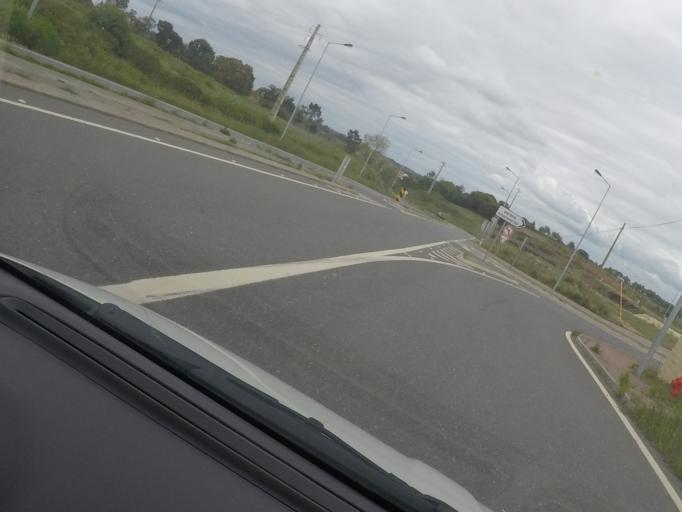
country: PT
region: Setubal
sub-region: Santiago do Cacem
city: Cercal
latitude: 37.7962
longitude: -8.6864
